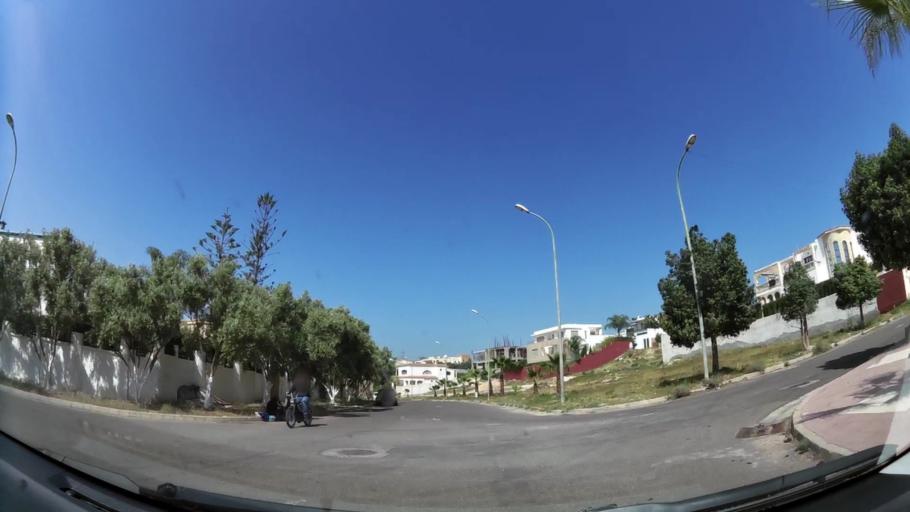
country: MA
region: Souss-Massa-Draa
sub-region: Agadir-Ida-ou-Tnan
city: Agadir
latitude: 30.4408
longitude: -9.5924
